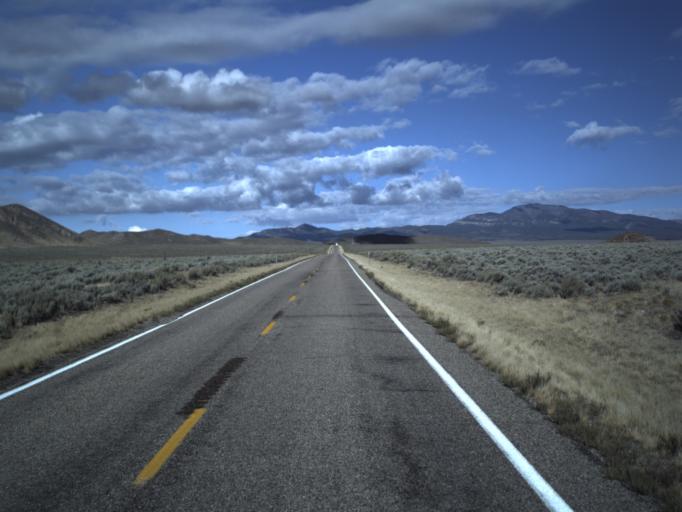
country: US
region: Utah
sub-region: Beaver County
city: Milford
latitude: 38.4147
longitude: -113.0785
